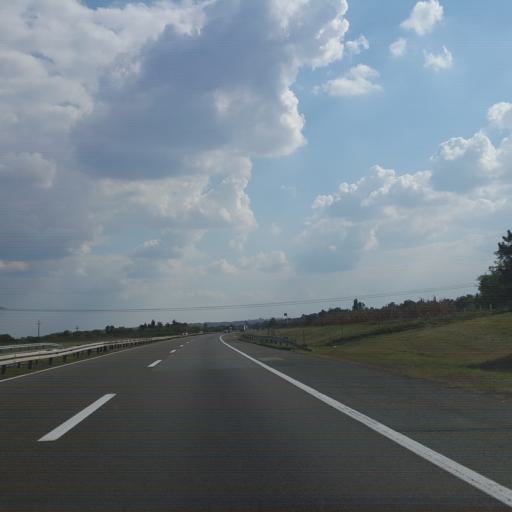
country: RS
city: Lugavcina
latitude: 44.5602
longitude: 20.9828
